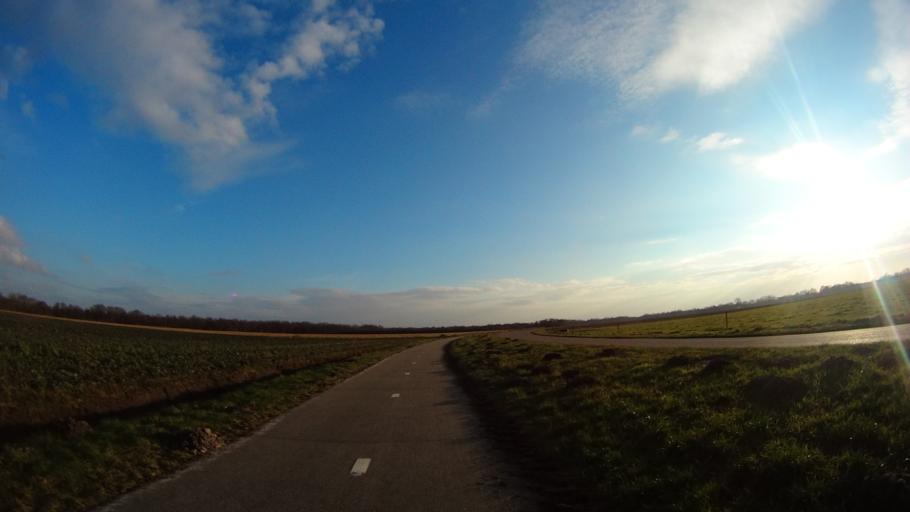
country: NL
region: Drenthe
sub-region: Gemeente Coevorden
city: Sleen
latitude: 52.8081
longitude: 6.7239
